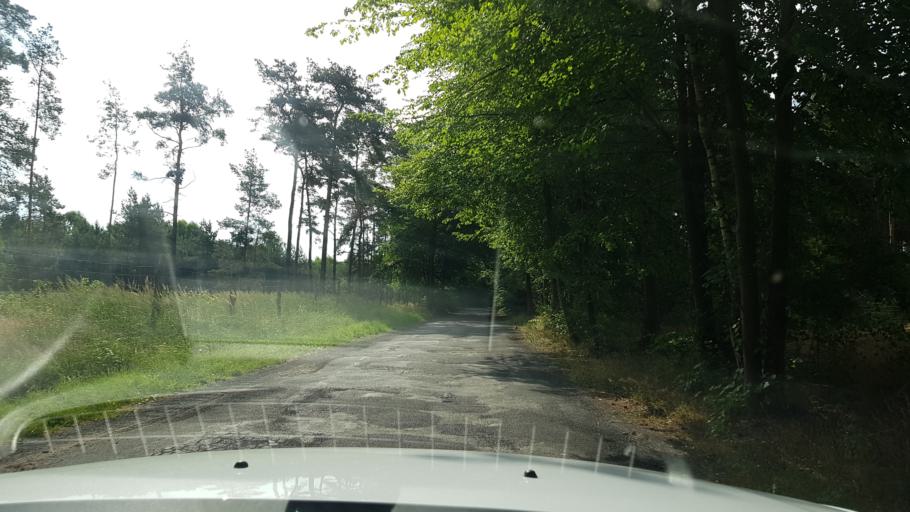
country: PL
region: West Pomeranian Voivodeship
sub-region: Powiat gryfinski
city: Gryfino
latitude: 53.2502
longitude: 14.5556
